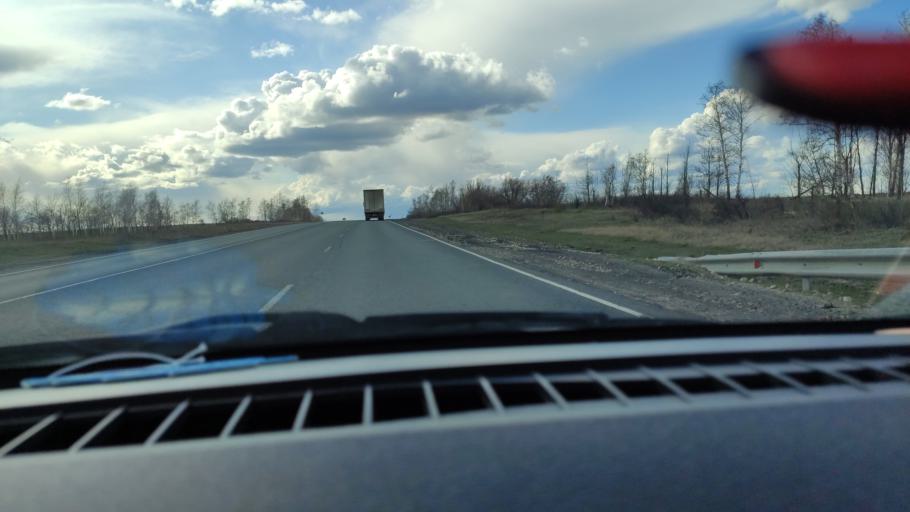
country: RU
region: Saratov
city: Shikhany
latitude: 52.1221
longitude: 47.2576
